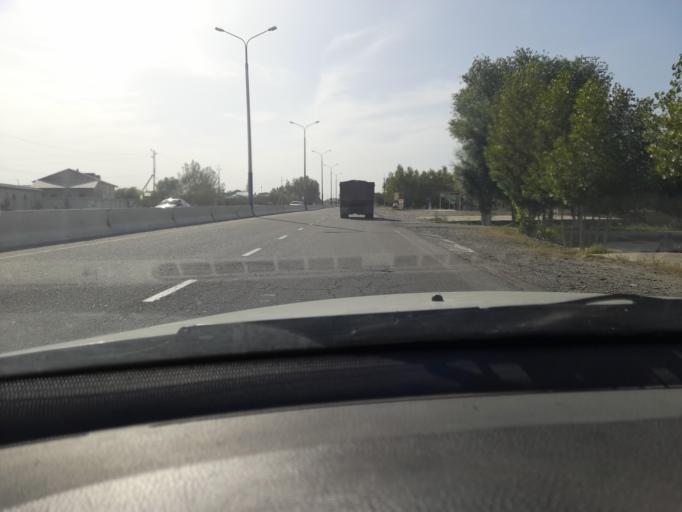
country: UZ
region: Samarqand
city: Kattaqo'rg'on
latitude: 39.9218
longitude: 66.2892
